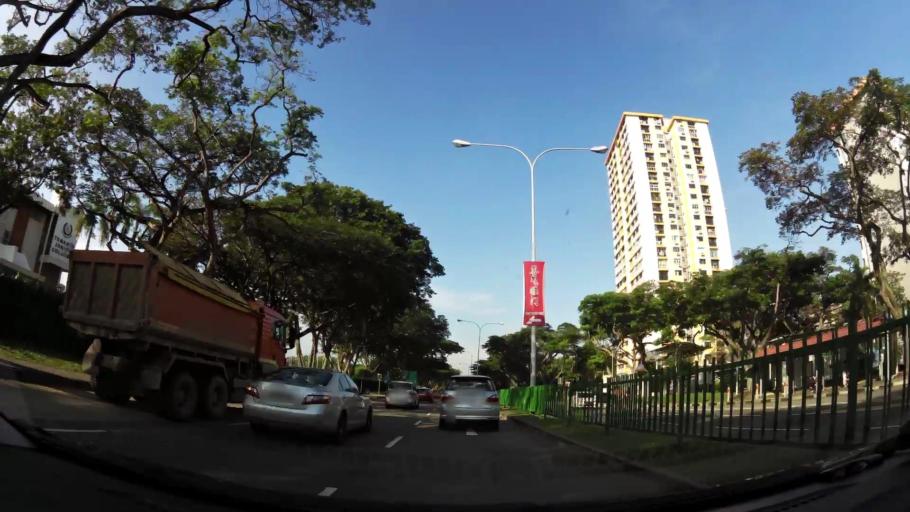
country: SG
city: Singapore
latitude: 1.3195
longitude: 103.9352
